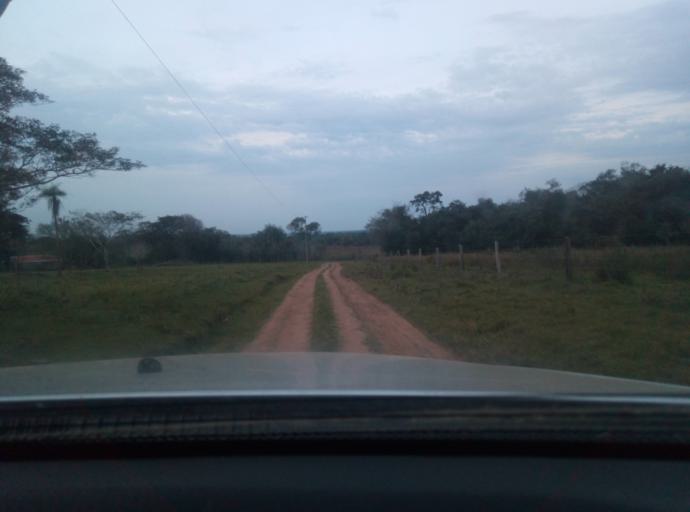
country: PY
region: Caaguazu
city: Carayao
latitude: -25.1472
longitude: -56.3829
